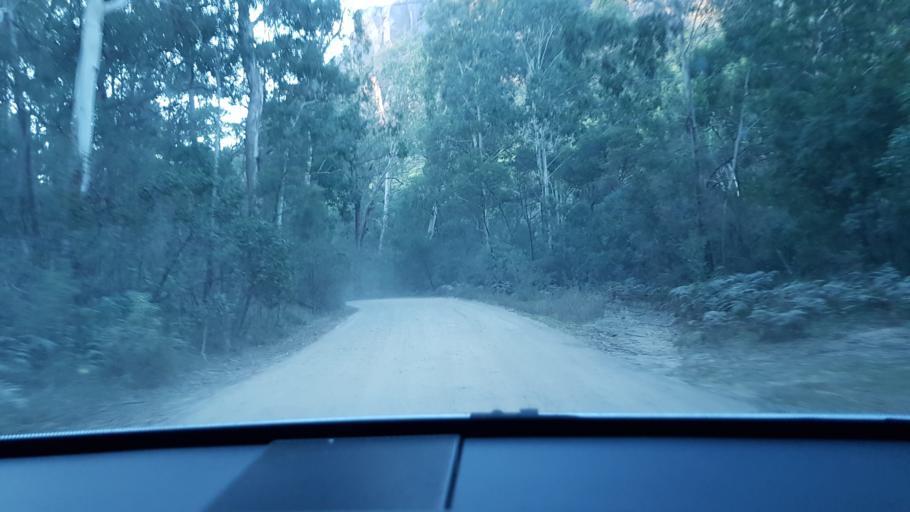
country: AU
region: New South Wales
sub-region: Lithgow
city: Portland
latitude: -33.1873
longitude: 150.2447
